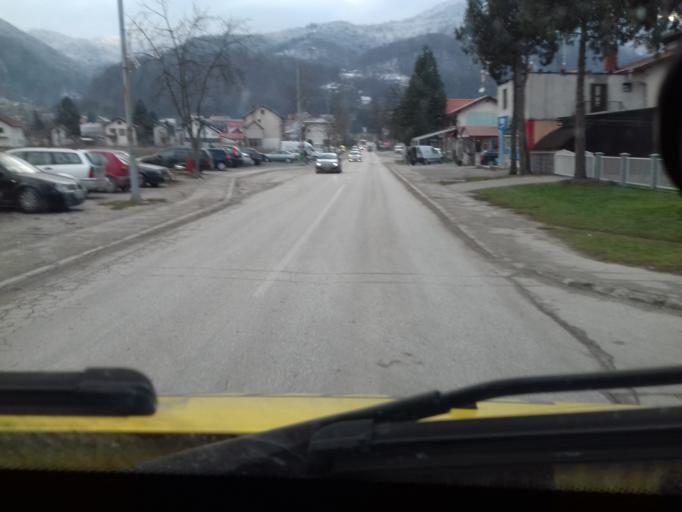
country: BA
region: Federation of Bosnia and Herzegovina
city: Zepce
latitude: 44.4266
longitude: 18.0405
